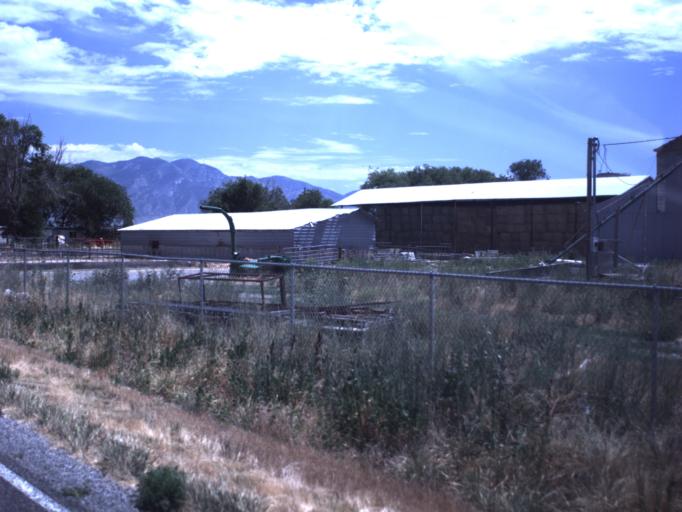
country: US
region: Utah
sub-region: Box Elder County
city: Tremonton
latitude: 41.7107
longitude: -112.2119
